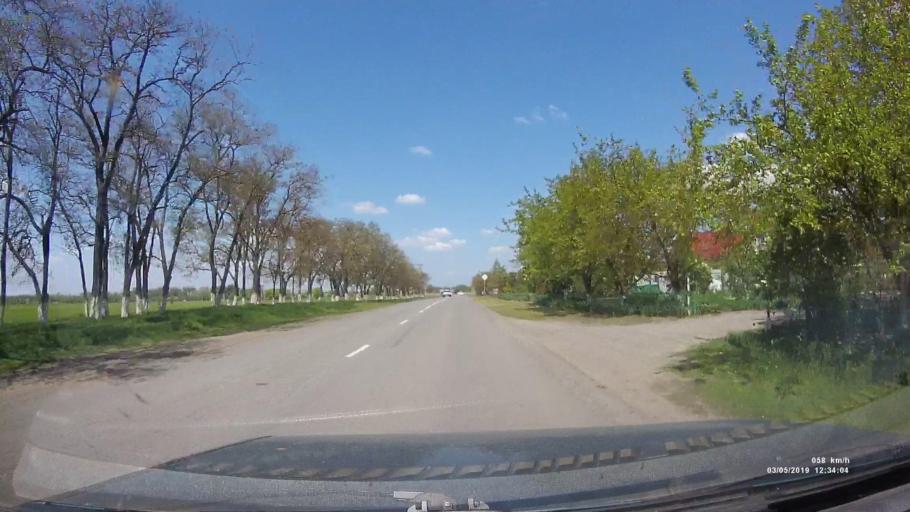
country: RU
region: Rostov
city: Semikarakorsk
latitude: 47.5179
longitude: 40.7705
